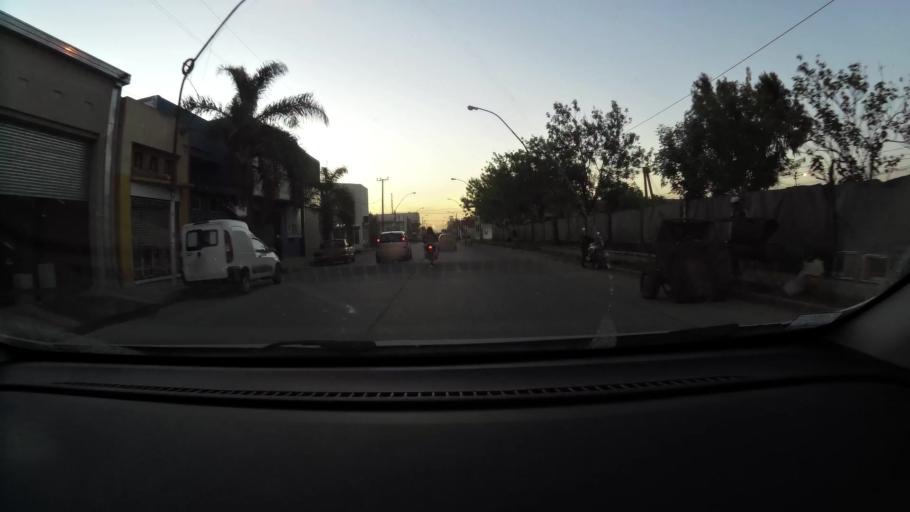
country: AR
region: Santa Fe
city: Santa Fe de la Vera Cruz
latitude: -31.6026
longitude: -60.7077
